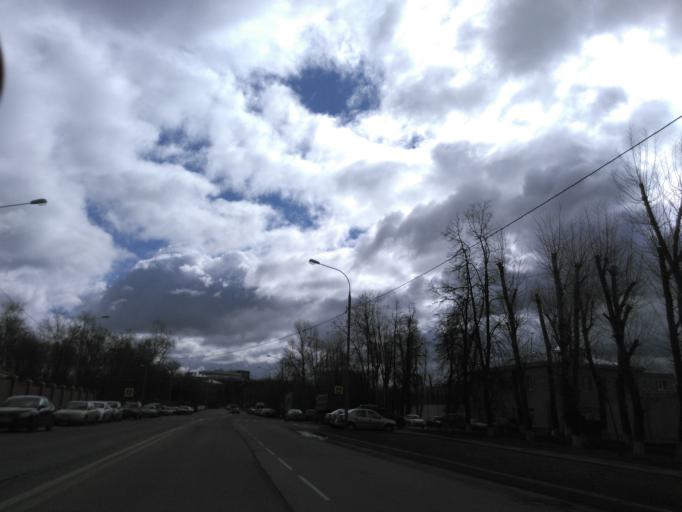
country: RU
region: Moscow
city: Golovinskiy
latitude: 55.8382
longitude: 37.4996
